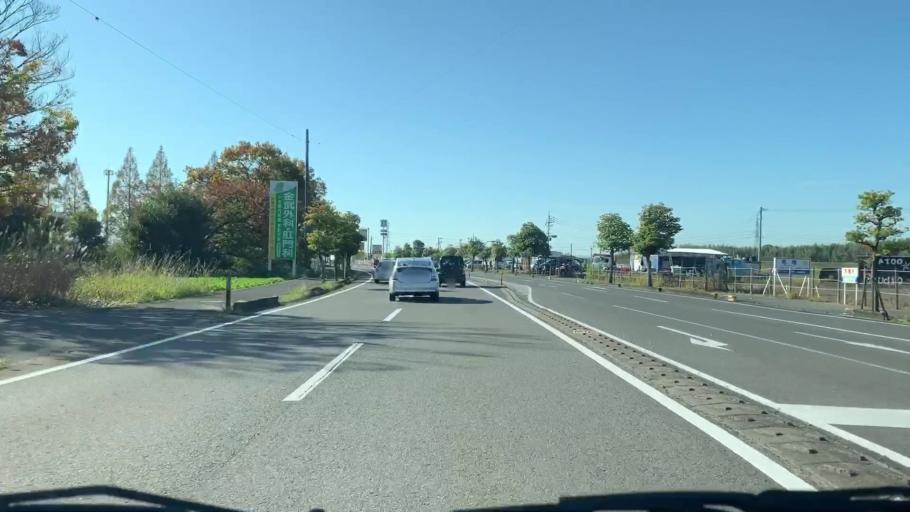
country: JP
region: Saga Prefecture
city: Saga-shi
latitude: 33.3146
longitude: 130.2759
